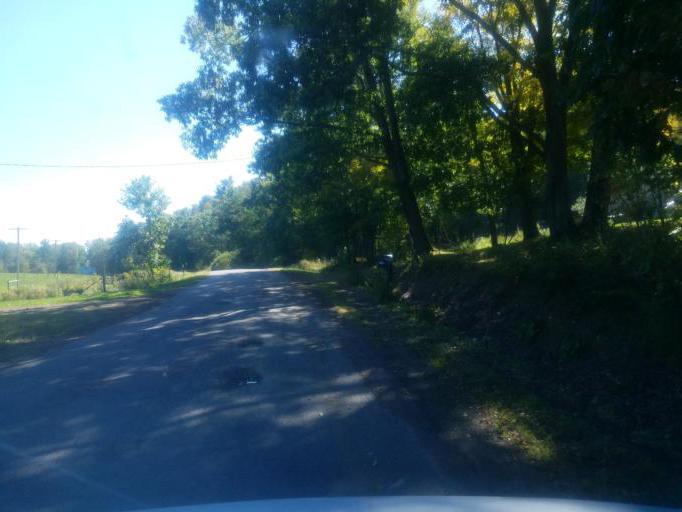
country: US
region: New York
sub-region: Allegany County
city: Houghton
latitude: 42.3152
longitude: -78.2067
